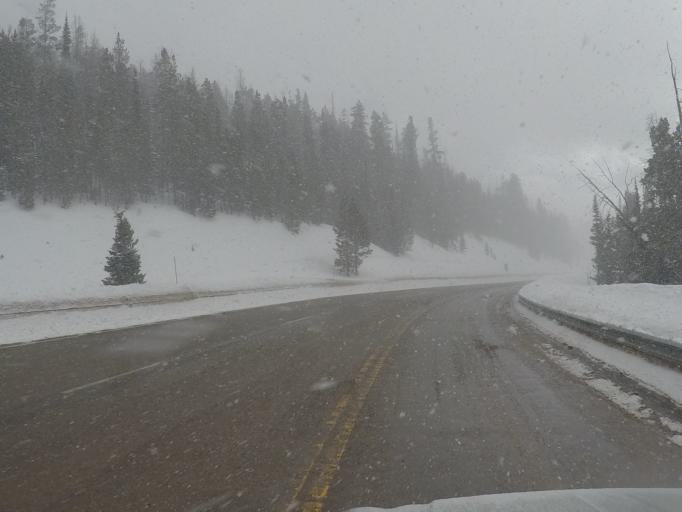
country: US
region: Montana
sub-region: Meagher County
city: White Sulphur Springs
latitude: 46.8331
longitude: -110.6946
